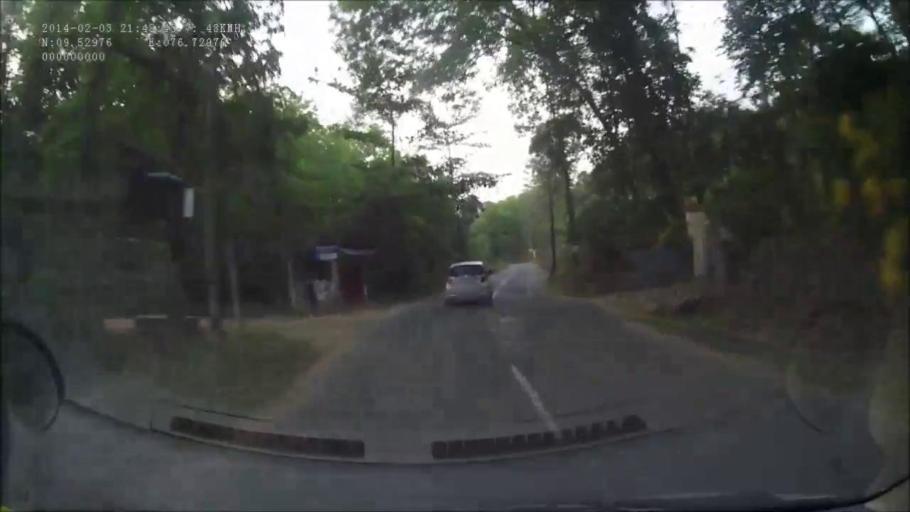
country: IN
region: Kerala
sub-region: Kottayam
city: Erattupetta
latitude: 9.5297
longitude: 76.7297
